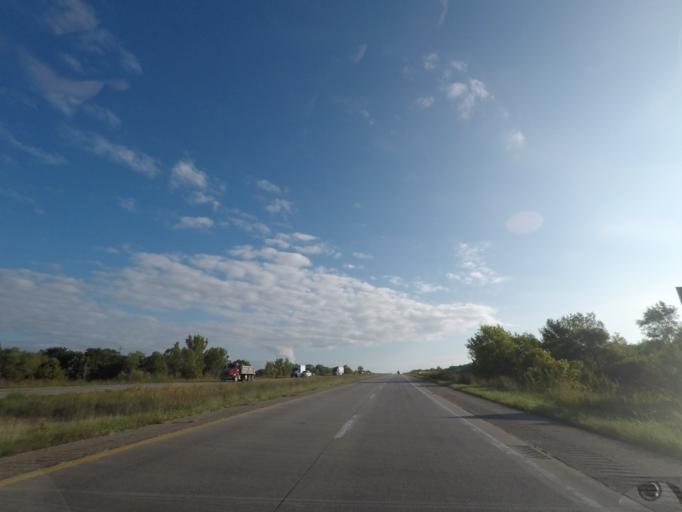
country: US
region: Iowa
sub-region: Polk County
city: Pleasant Hill
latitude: 41.5795
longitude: -93.5115
